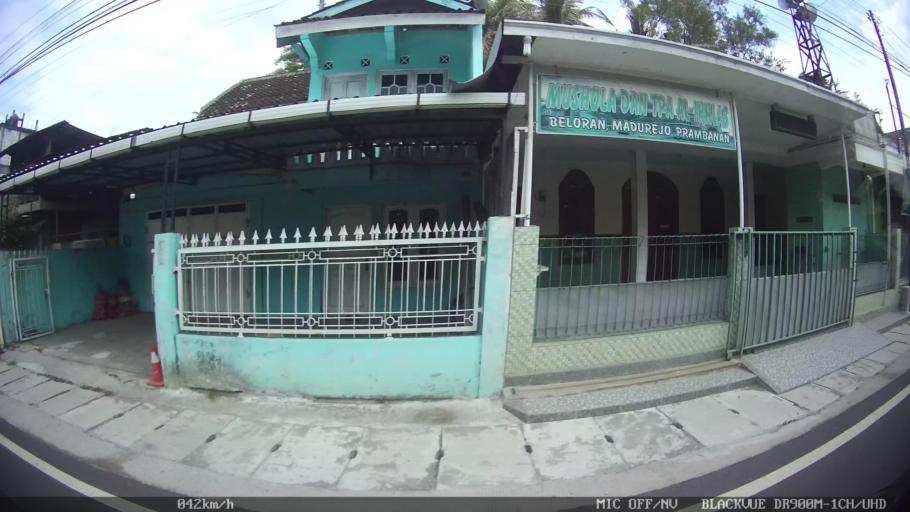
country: ID
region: Central Java
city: Candi Prambanan
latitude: -7.8038
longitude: 110.4828
